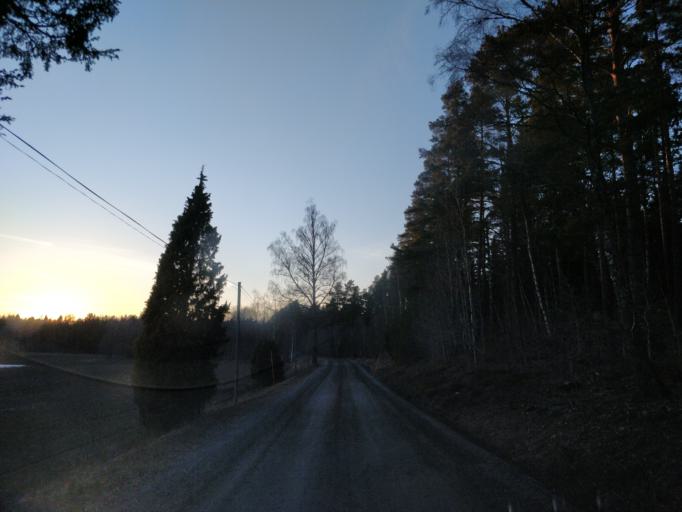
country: SE
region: Uppsala
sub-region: Enkopings Kommun
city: Orsundsbro
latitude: 59.8257
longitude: 17.1503
